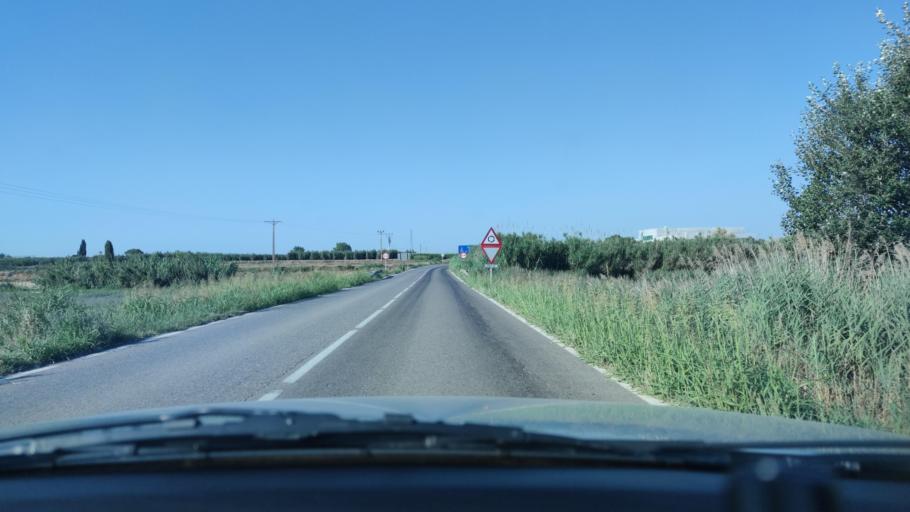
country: ES
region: Catalonia
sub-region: Provincia de Lleida
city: Sidamon
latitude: 41.6401
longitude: 0.7937
